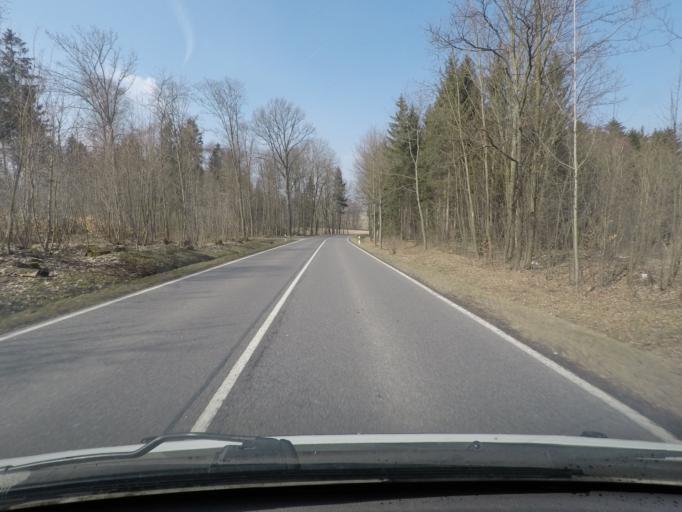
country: DE
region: Saxony
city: Grossschirma
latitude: 50.9504
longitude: 13.2942
